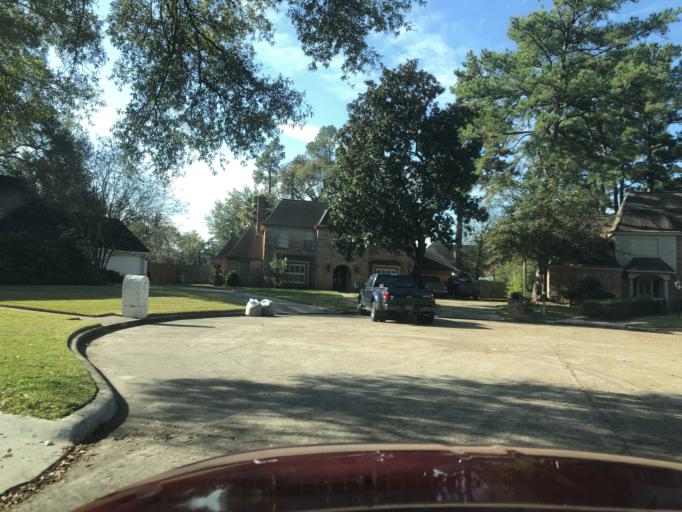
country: US
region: Texas
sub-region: Harris County
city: Spring
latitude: 30.0132
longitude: -95.4632
